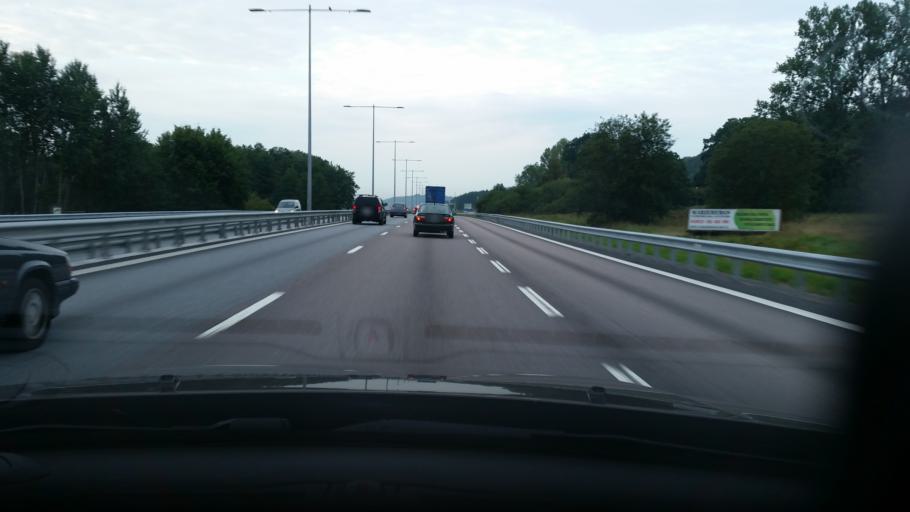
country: SE
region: Vaestra Goetaland
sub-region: Ale Kommun
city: Surte
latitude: 57.8361
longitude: 12.0057
